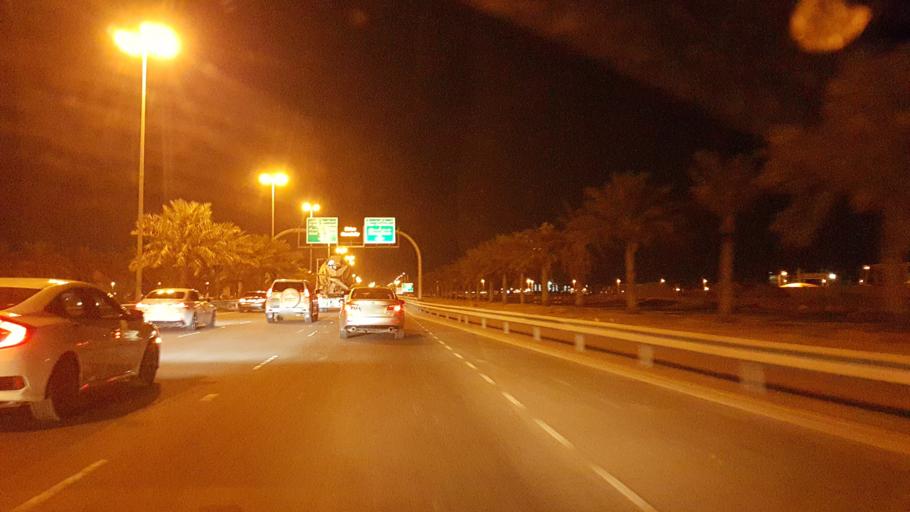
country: BH
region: Muharraq
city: Al Hadd
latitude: 26.2488
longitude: 50.6591
